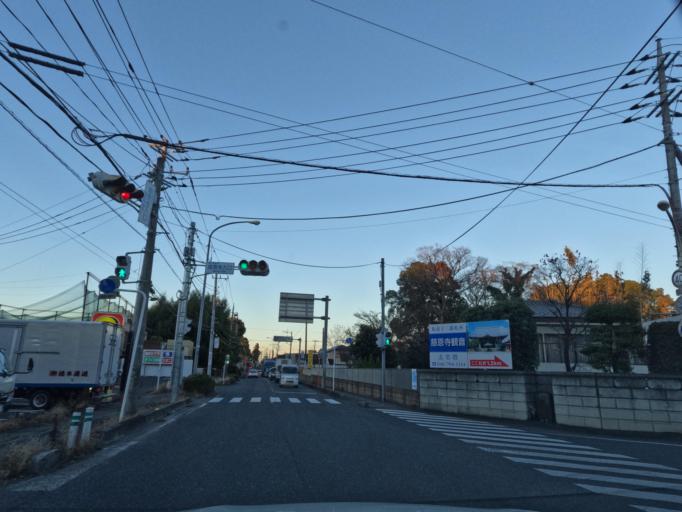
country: JP
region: Saitama
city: Iwatsuki
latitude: 35.9830
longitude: 139.6990
